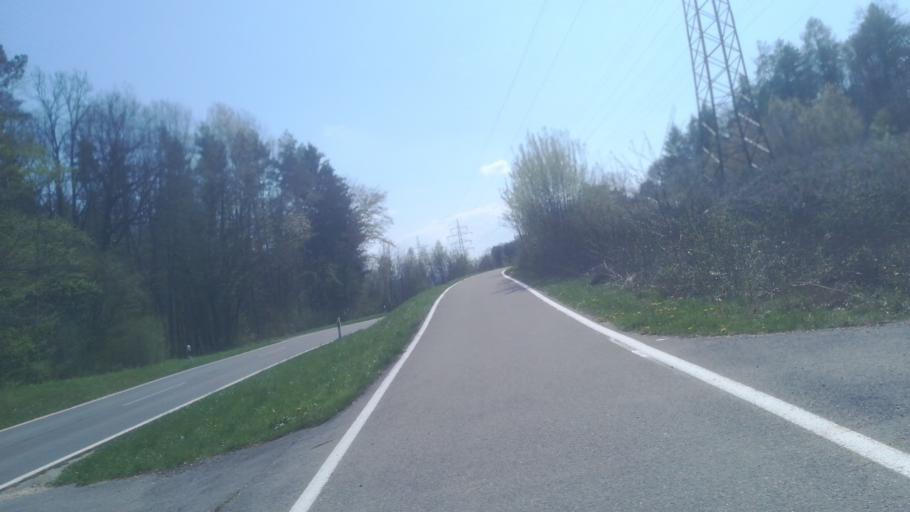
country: DE
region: Baden-Wuerttemberg
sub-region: Freiburg Region
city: Singen
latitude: 47.7756
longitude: 8.8632
